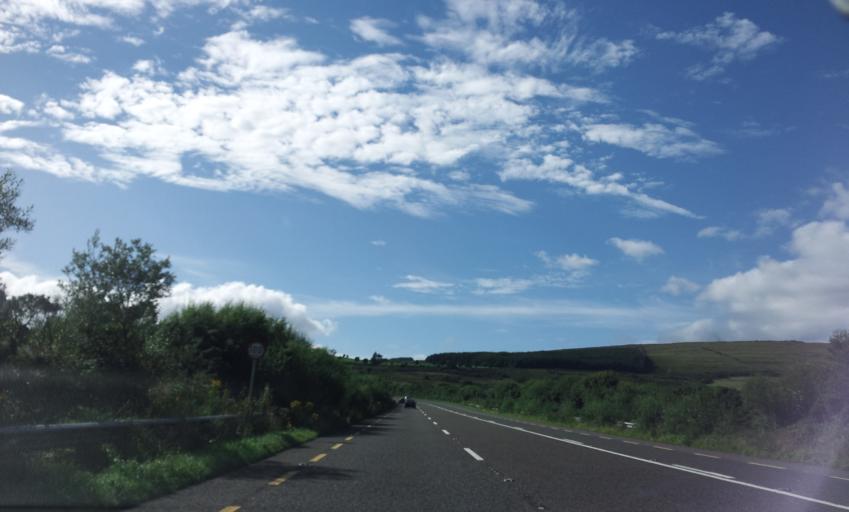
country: IE
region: Munster
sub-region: County Cork
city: Millstreet
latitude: 51.9614
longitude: -9.2040
